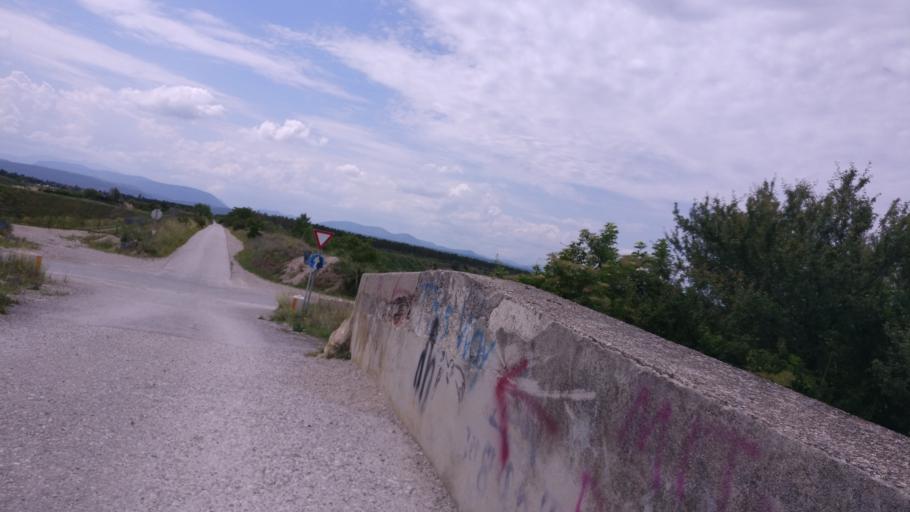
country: AT
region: Lower Austria
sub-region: Politischer Bezirk Wiener Neustadt
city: Sollenau
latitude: 47.8825
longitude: 16.2801
